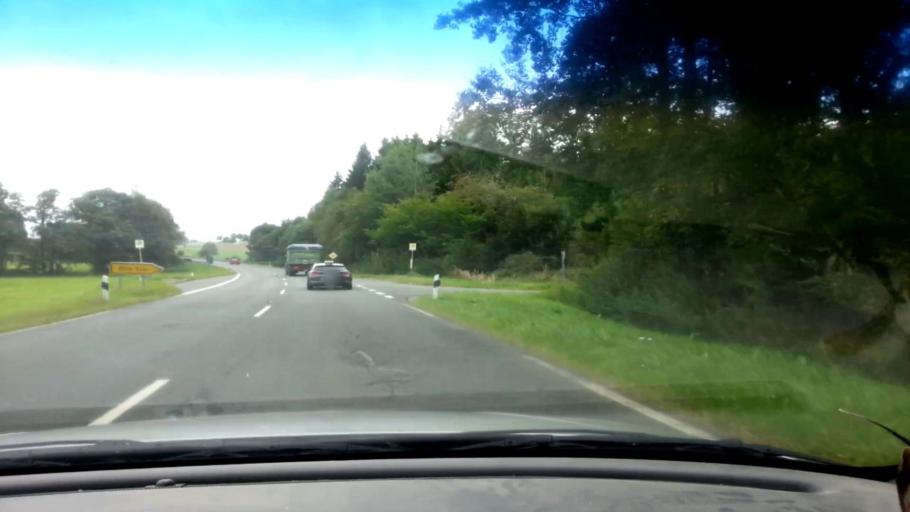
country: DE
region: Bavaria
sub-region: Upper Franconia
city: Grub
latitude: 50.0867
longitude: 11.9342
